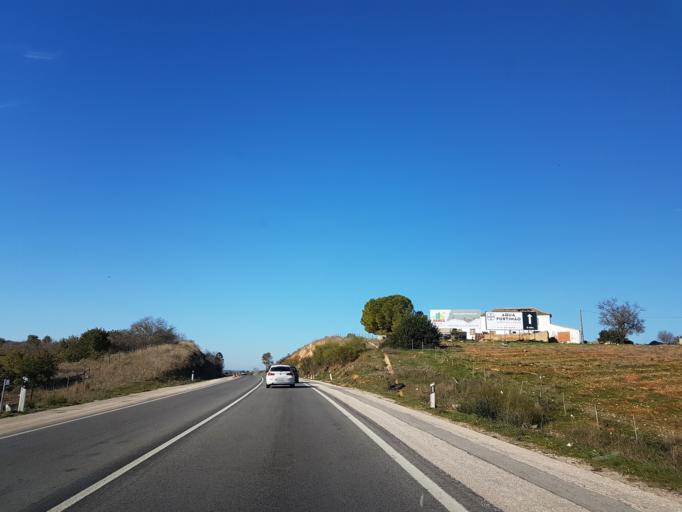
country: PT
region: Faro
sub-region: Lagoa
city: Estombar
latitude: 37.1517
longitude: -8.4833
